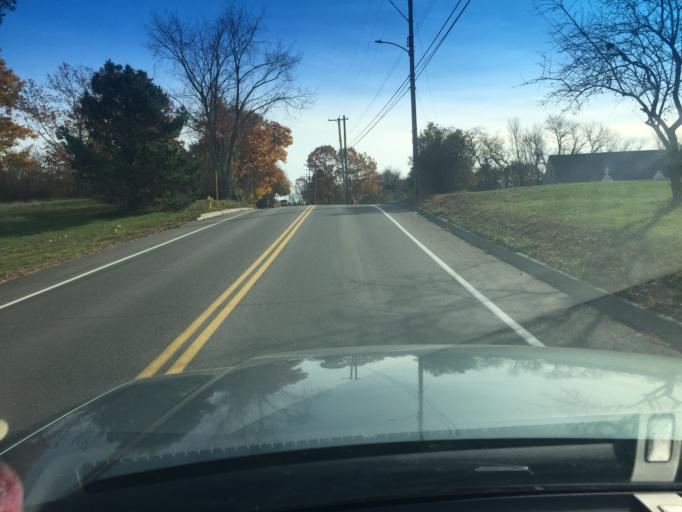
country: US
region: Maine
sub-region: York County
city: York Harbor
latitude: 43.1604
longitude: -70.7035
